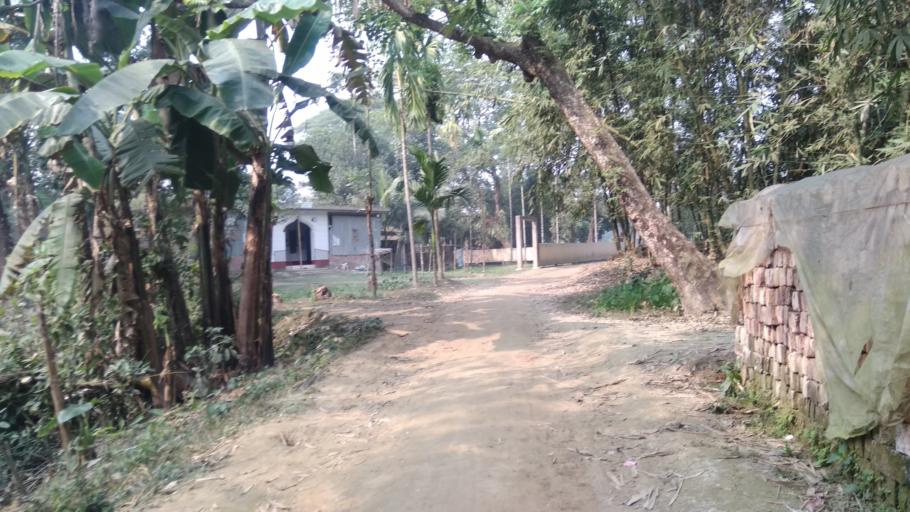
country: BD
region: Dhaka
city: Netrakona
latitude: 24.8918
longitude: 90.6651
